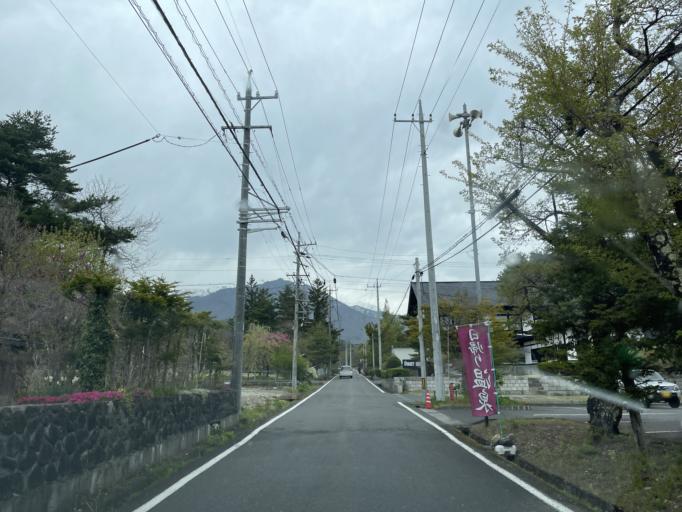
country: JP
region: Nagano
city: Omachi
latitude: 36.5179
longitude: 137.8093
